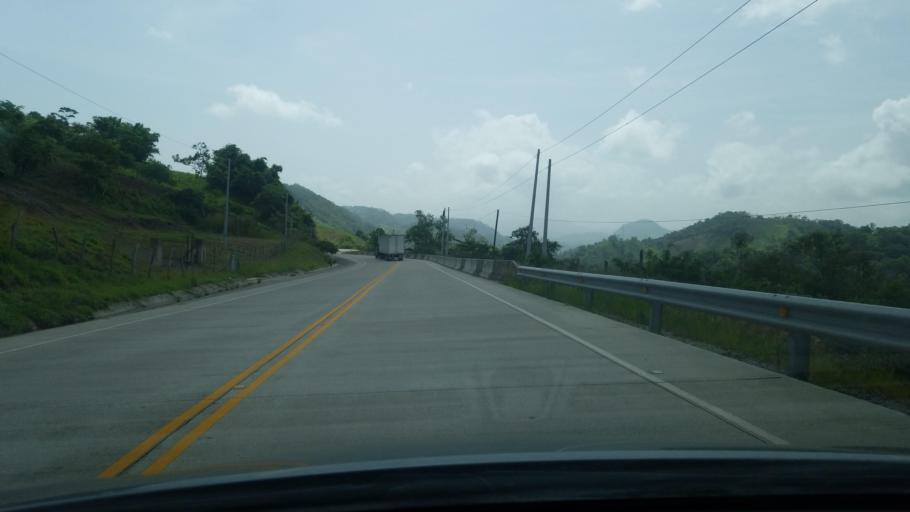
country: HN
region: Copan
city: San Jeronimo
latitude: 14.9552
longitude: -88.9029
